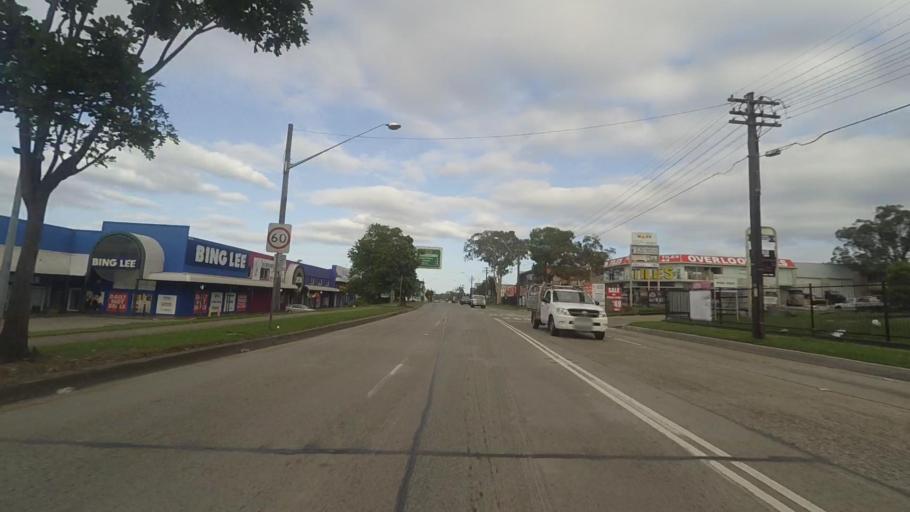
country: AU
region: New South Wales
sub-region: Bankstown
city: Bankstown
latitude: -33.9338
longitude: 151.0282
